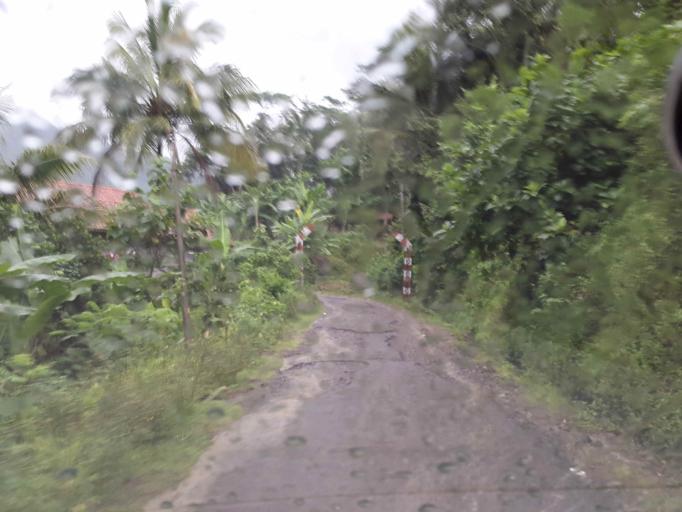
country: ID
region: Central Java
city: Kadumanis
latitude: -7.1703
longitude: 108.9017
